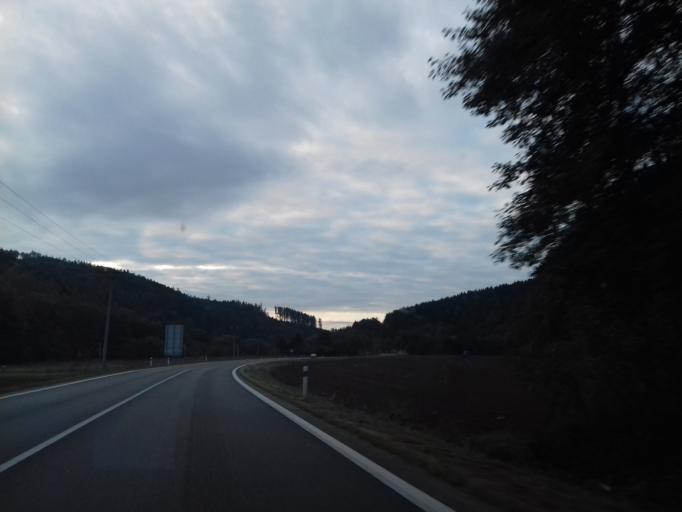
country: CZ
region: Zlin
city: Bojkovice
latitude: 48.9485
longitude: 17.9042
